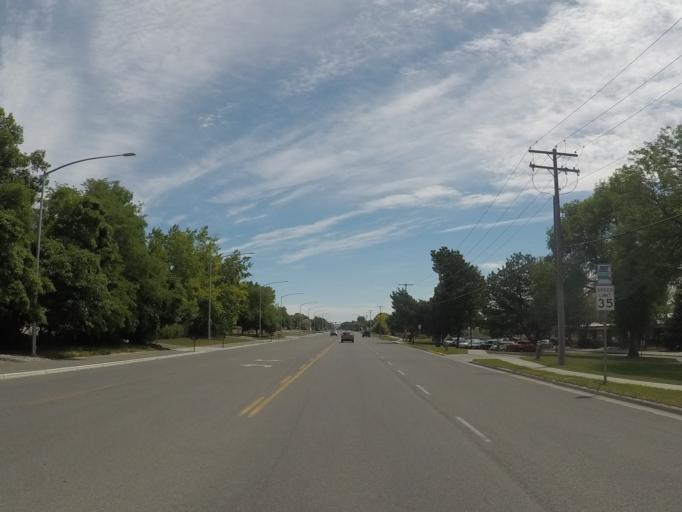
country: US
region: Montana
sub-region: Yellowstone County
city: Billings
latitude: 45.7985
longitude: -108.6166
